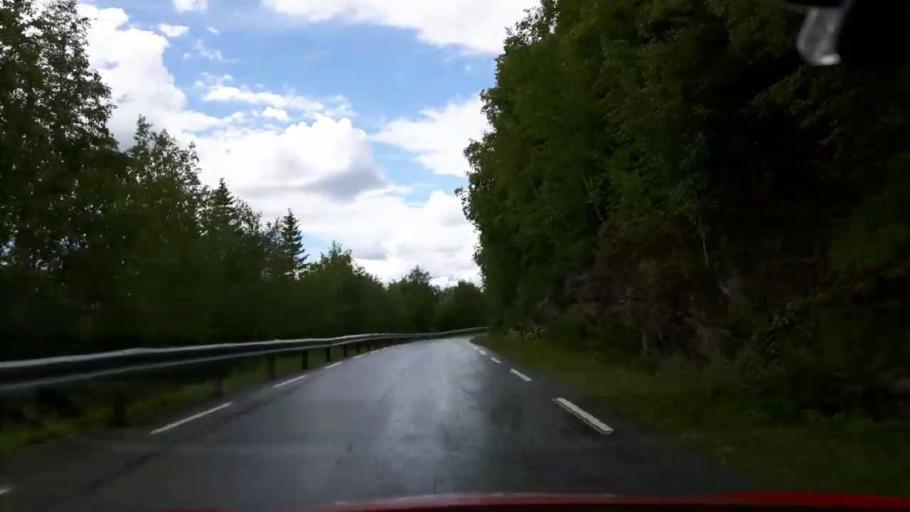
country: NO
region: Nord-Trondelag
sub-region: Lierne
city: Sandvika
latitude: 64.1067
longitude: 13.9857
